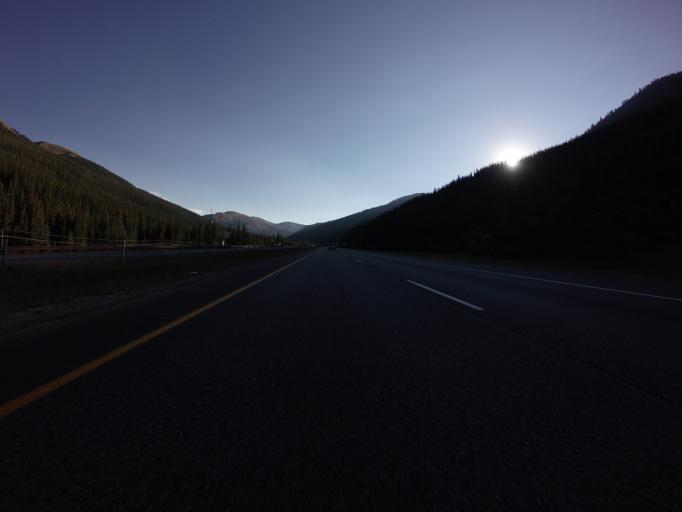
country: US
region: Colorado
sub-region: Summit County
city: Keystone
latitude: 39.7004
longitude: -105.8656
